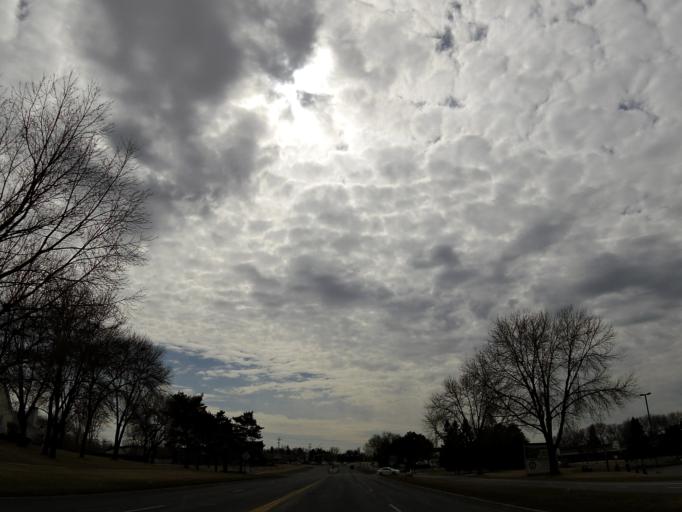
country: US
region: Minnesota
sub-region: Scott County
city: Savage
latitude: 44.8108
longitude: -93.3840
